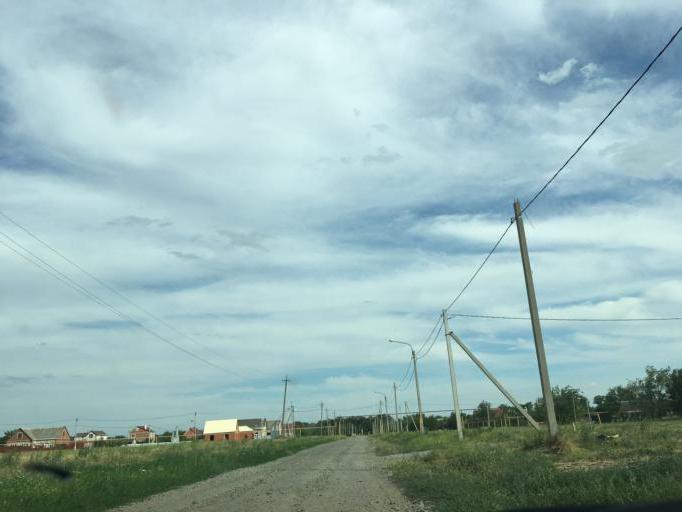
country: RU
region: Krasnodarskiy
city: Kushchevskaya
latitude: 46.5523
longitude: 39.6688
